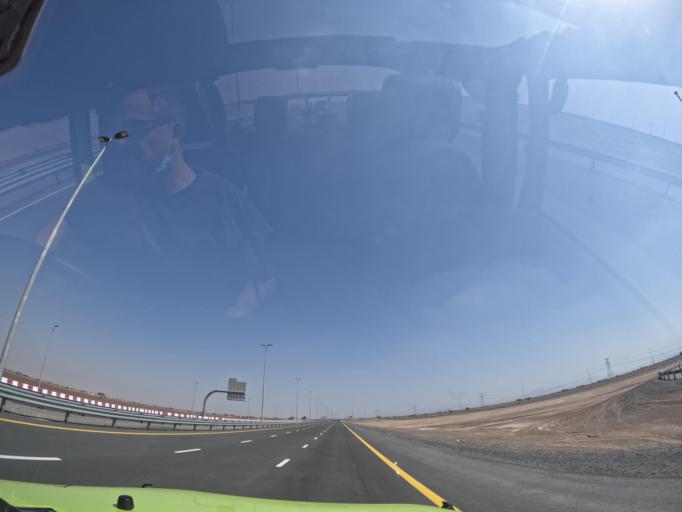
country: AE
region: Ash Shariqah
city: Adh Dhayd
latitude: 24.9318
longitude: 55.8170
